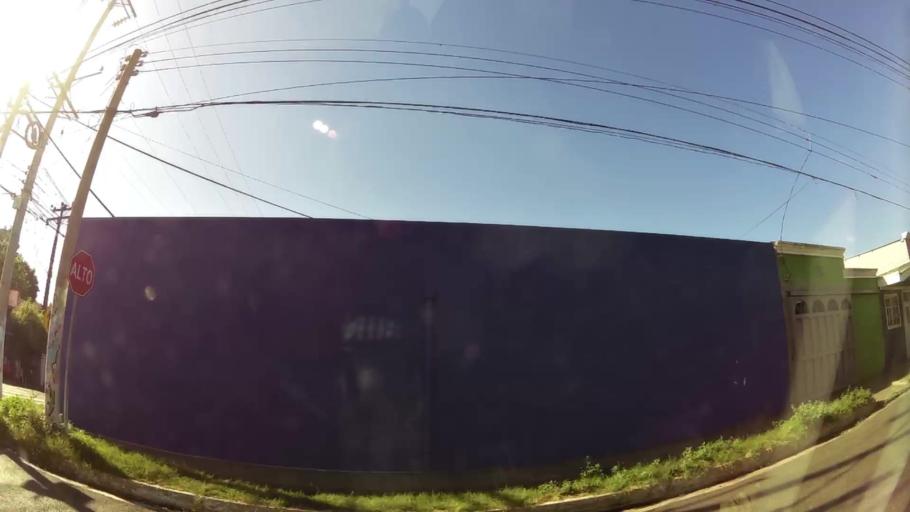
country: SV
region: Sonsonate
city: Sonzacate
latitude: 13.7372
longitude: -89.7152
